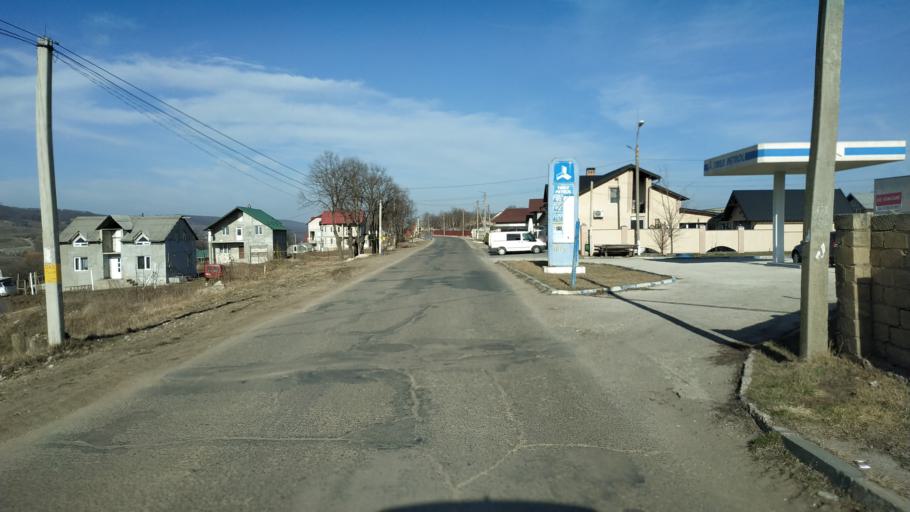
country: MD
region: Chisinau
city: Vatra
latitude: 47.0191
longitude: 28.6502
